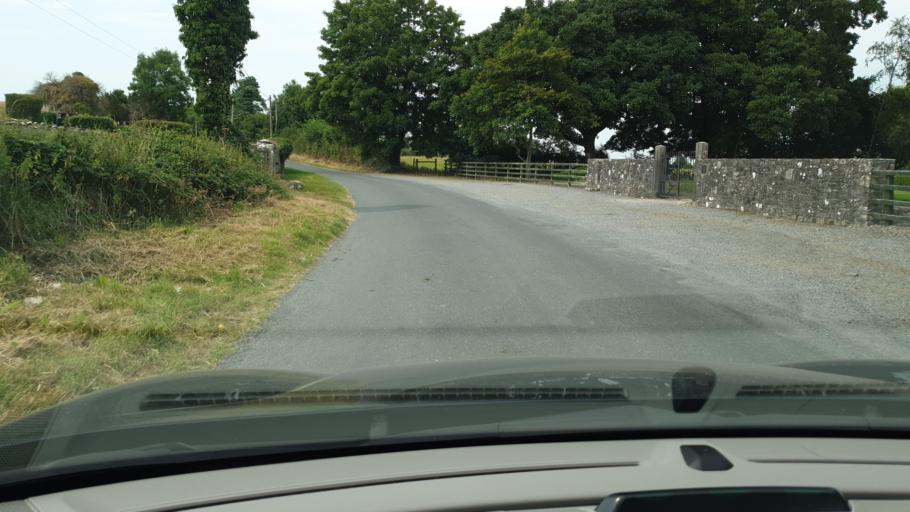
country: IE
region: Leinster
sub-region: An Mhi
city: Athboy
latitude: 53.6664
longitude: -6.9231
